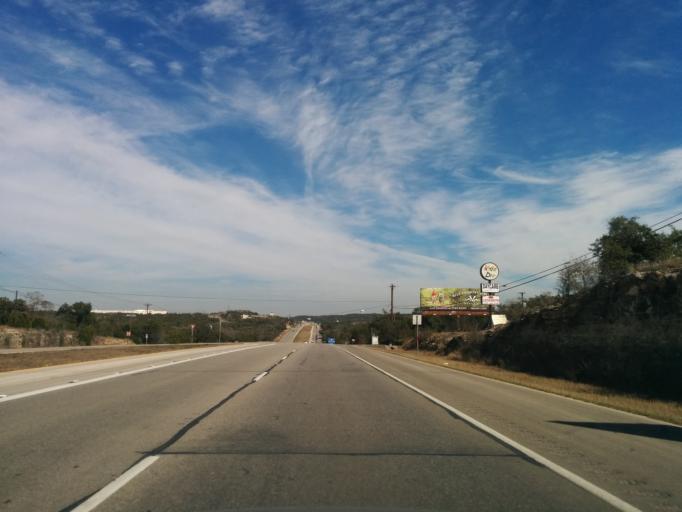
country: US
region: Texas
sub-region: Comal County
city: Bulverde
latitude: 29.7816
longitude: -98.4240
